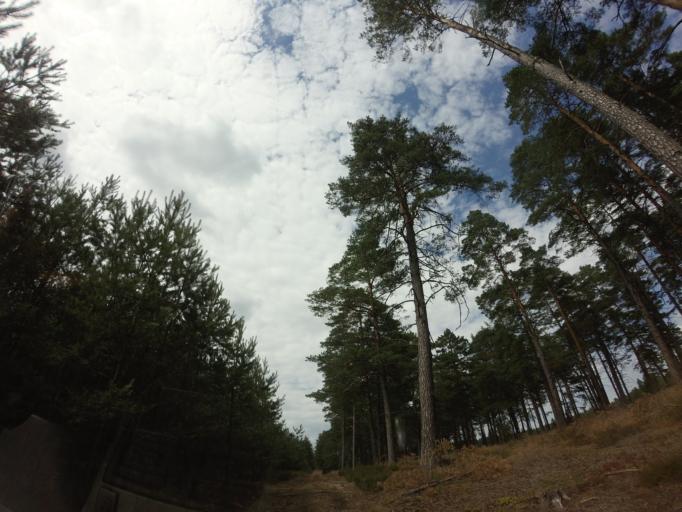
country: PL
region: West Pomeranian Voivodeship
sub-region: Powiat choszczenski
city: Drawno
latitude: 53.1624
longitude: 15.7499
